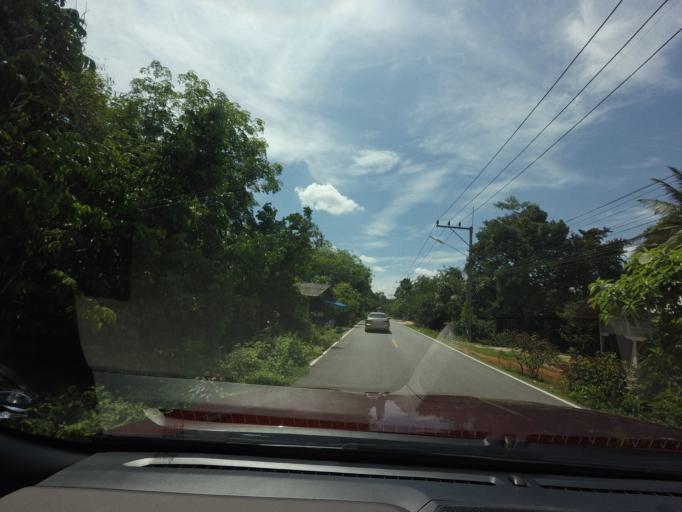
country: TH
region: Narathiwat
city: Ra-ngae
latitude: 6.2860
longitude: 101.6854
